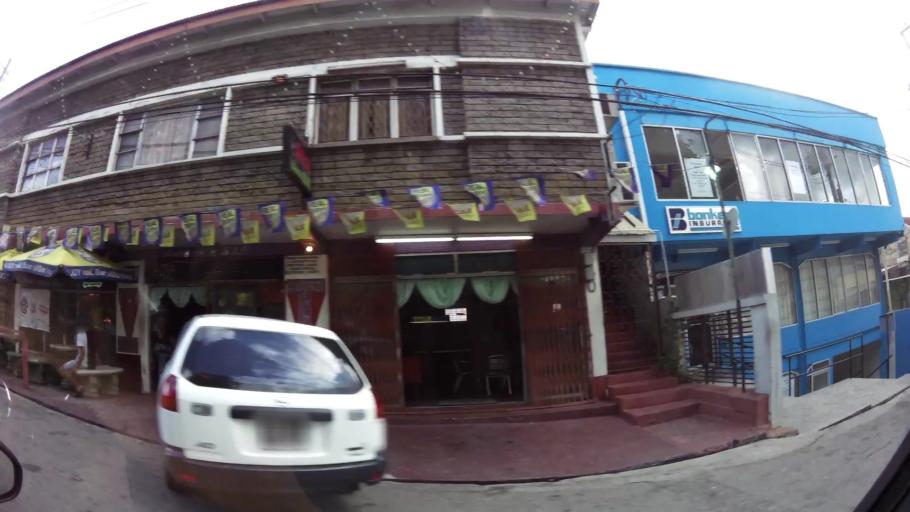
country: TT
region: City of San Fernando
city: San Fernando
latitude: 10.2783
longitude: -61.4585
